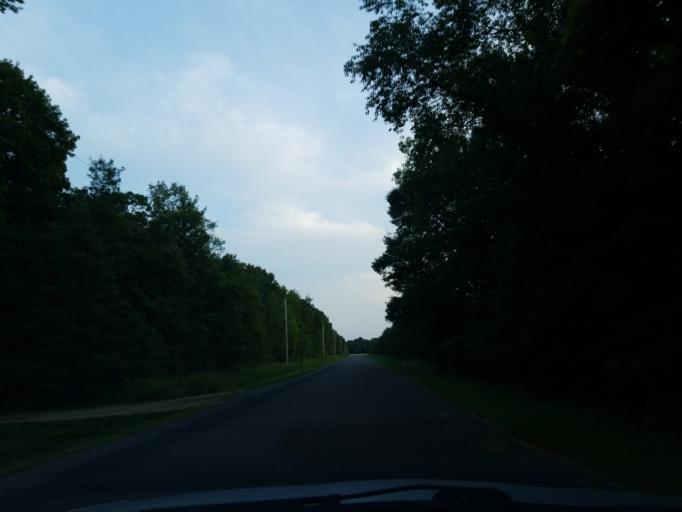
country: US
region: Minnesota
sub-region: Washington County
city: Stillwater
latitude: 45.0783
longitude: -92.7713
